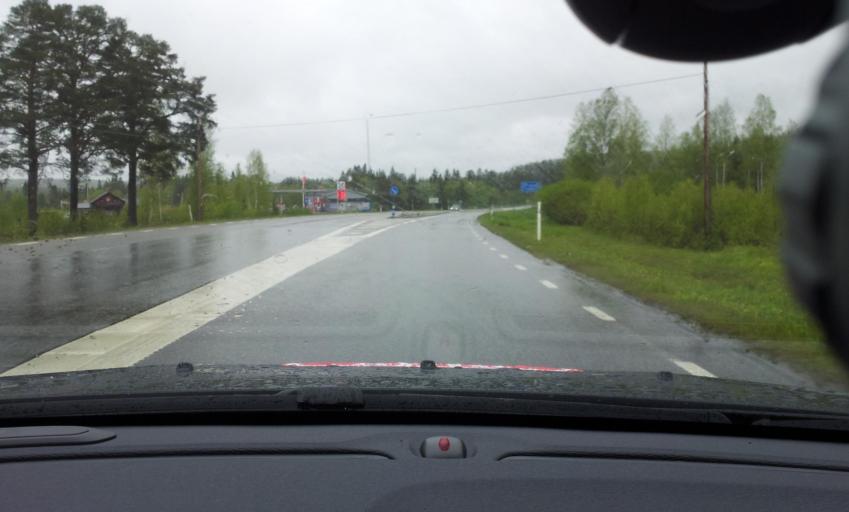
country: SE
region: Jaemtland
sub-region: Bergs Kommun
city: Hoverberg
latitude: 62.7502
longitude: 14.4270
